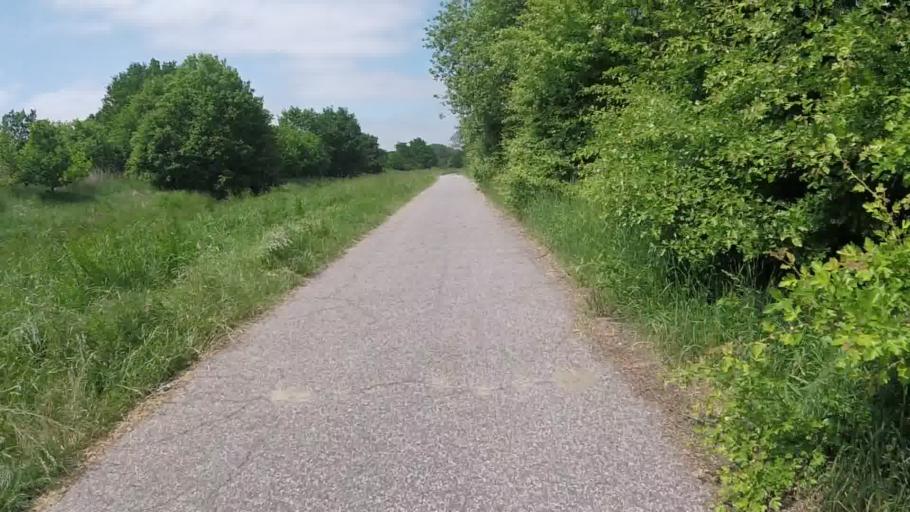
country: DE
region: Schleswig-Holstein
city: Oststeinbek
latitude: 53.4920
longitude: 10.1509
